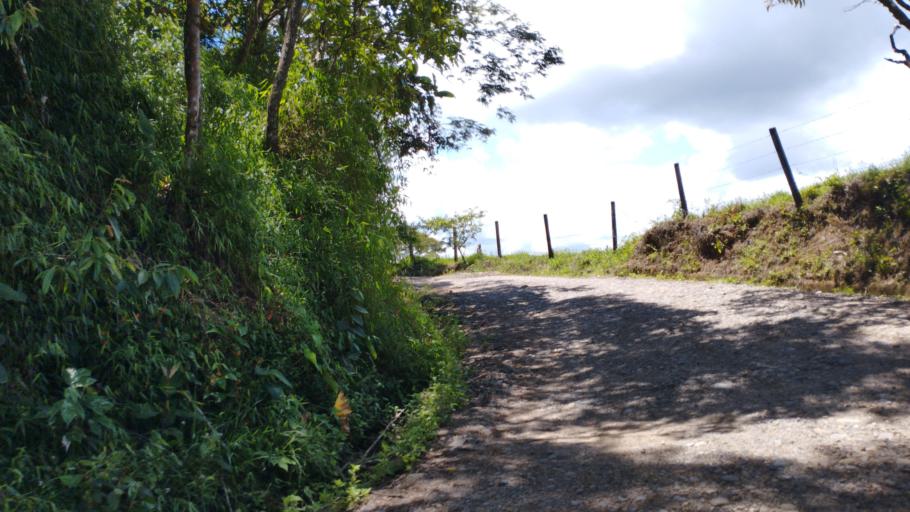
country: CO
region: Boyaca
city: San Luis de Gaceno
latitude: 4.7501
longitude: -73.1453
